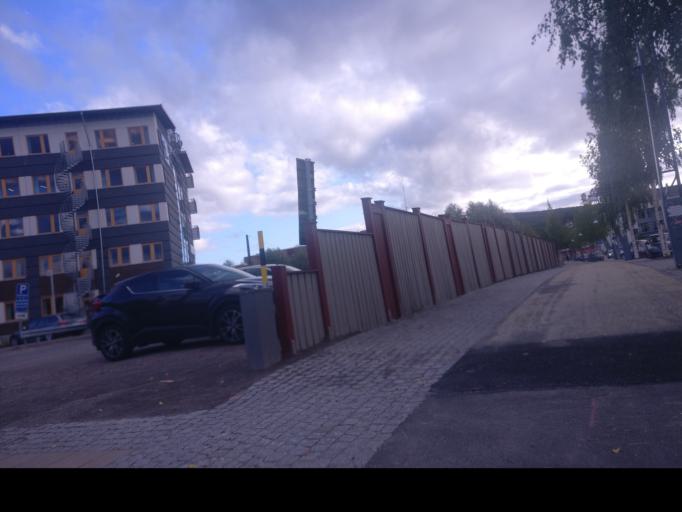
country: SE
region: Vaesternorrland
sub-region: Sundsvalls Kommun
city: Sundsvall
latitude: 62.3907
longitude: 17.3172
